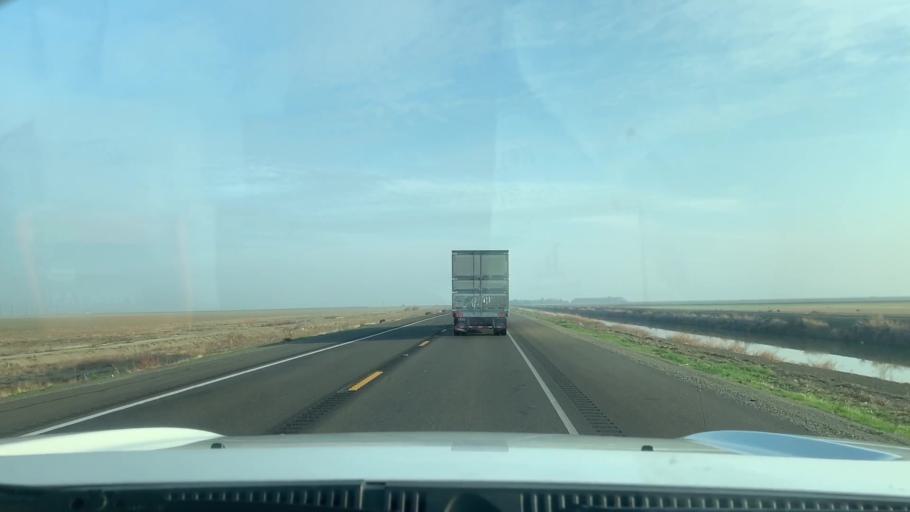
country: US
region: California
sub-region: Kings County
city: Kettleman City
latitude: 36.0406
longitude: -119.9556
